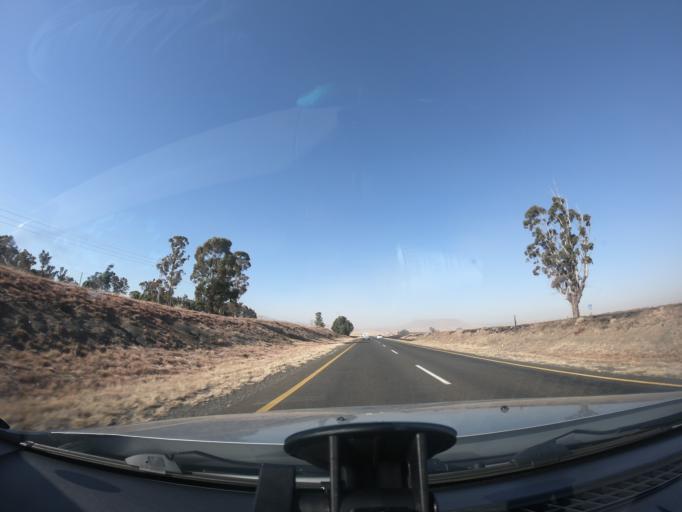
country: ZA
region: Mpumalanga
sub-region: Gert Sibande District Municipality
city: Volksrust
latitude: -27.2335
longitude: 29.8883
